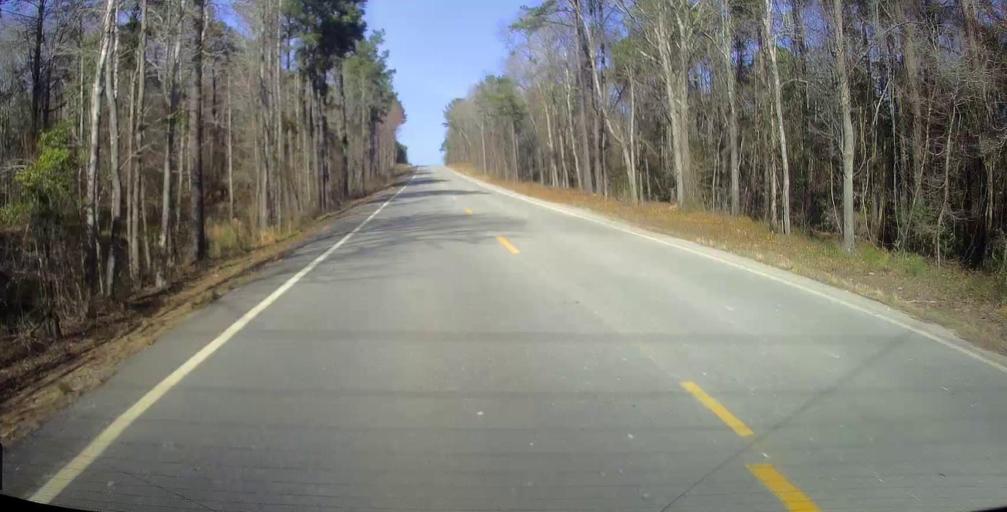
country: US
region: Georgia
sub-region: Wilkinson County
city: Gordon
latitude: 32.8008
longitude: -83.3288
